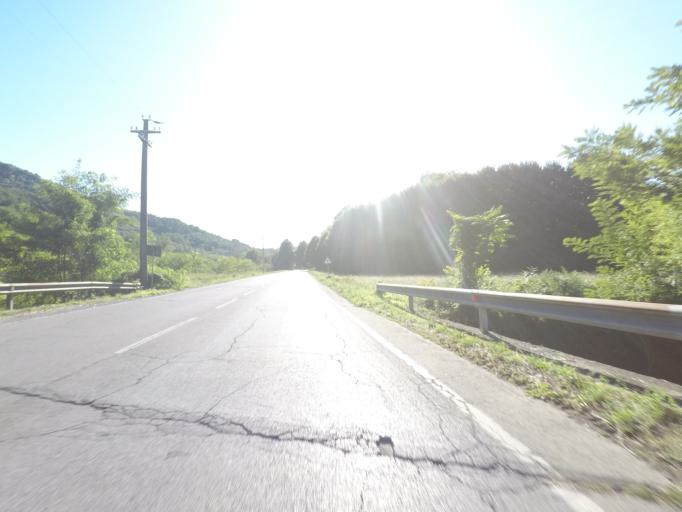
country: IT
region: Tuscany
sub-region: Provincia di Lucca
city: San Martino in Freddana-Monsagrati
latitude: 43.9032
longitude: 10.4125
